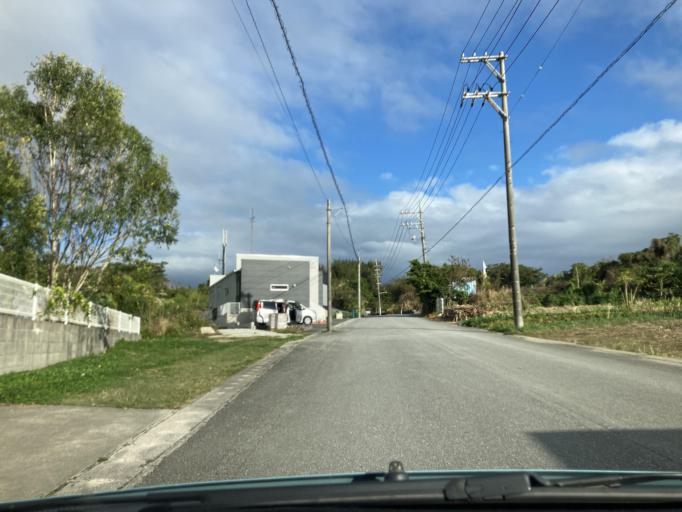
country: JP
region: Okinawa
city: Itoman
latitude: 26.1151
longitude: 127.6789
